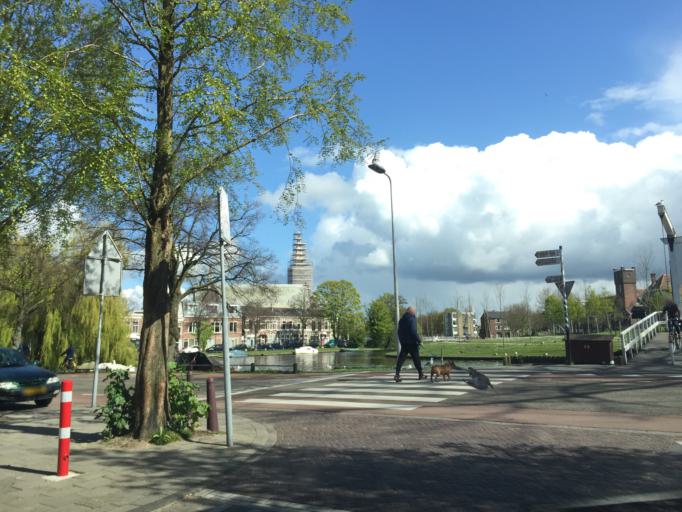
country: NL
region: South Holland
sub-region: Gemeente Leiden
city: Leiden
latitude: 52.1645
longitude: 4.4978
